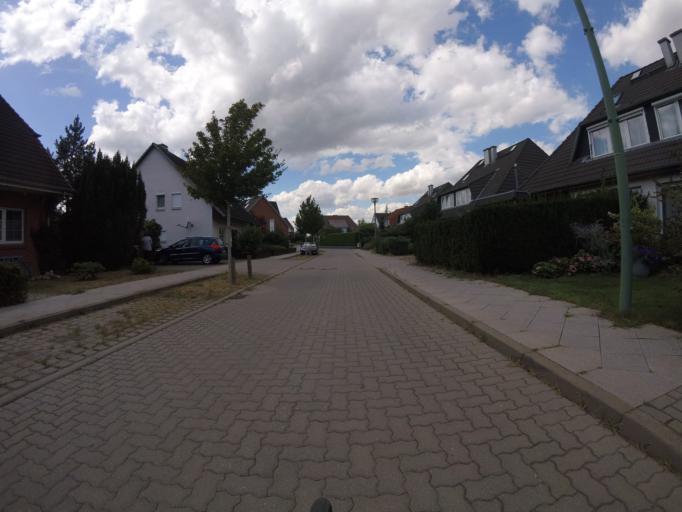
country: DE
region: Brandenburg
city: Werder
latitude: 52.4130
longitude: 12.9895
